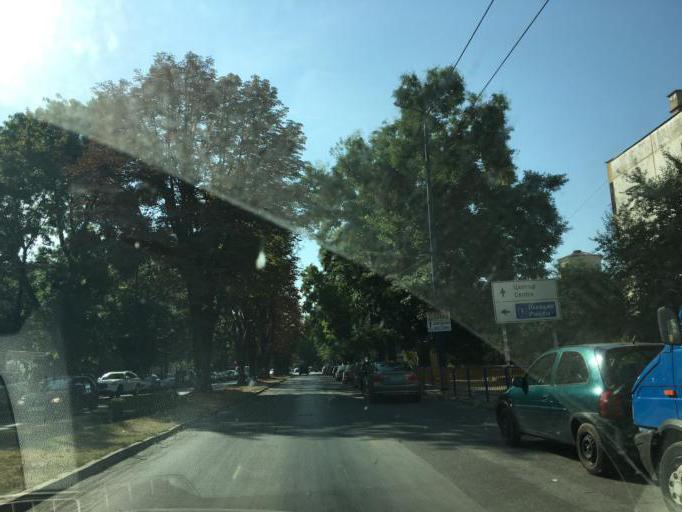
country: BG
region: Pazardzhik
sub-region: Obshtina Pazardzhik
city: Pazardzhik
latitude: 42.2012
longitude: 24.3322
